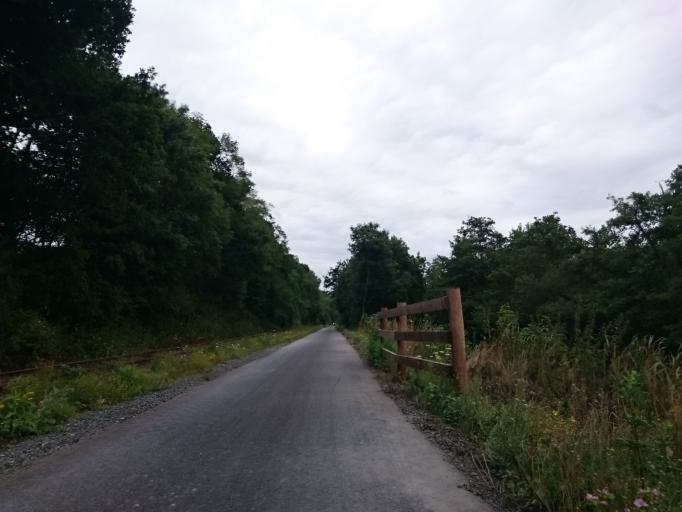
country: FR
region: Lower Normandy
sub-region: Departement du Calvados
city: Sainte-Honorine-du-Fay
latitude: 49.0565
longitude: -0.4595
